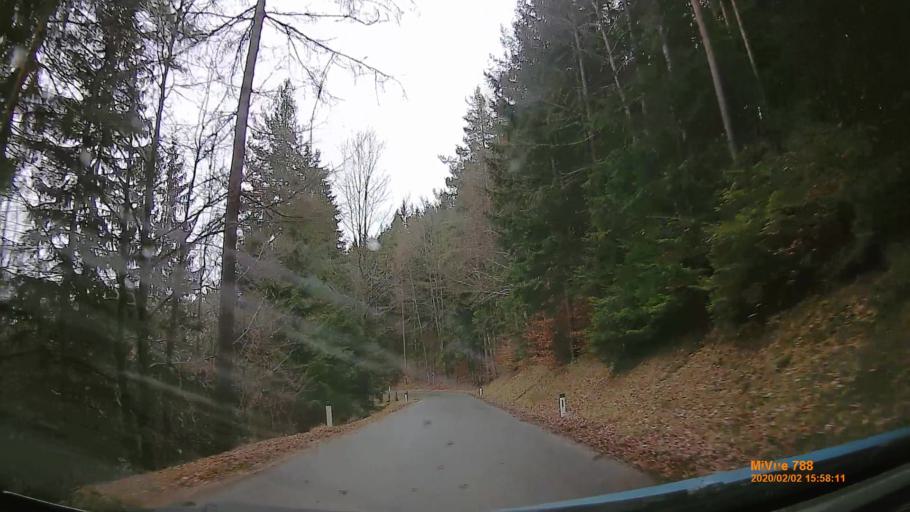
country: AT
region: Lower Austria
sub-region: Politischer Bezirk Neunkirchen
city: Semmering
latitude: 47.6602
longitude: 15.7958
